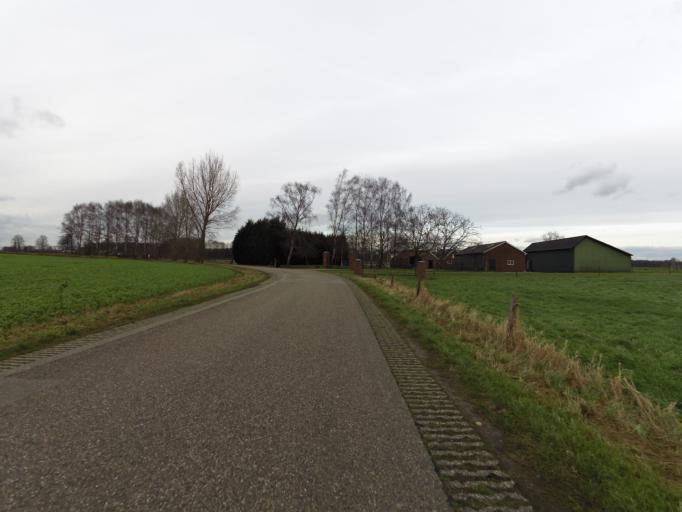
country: NL
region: Gelderland
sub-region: Oude IJsselstreek
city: Wisch
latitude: 51.9182
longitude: 6.3880
